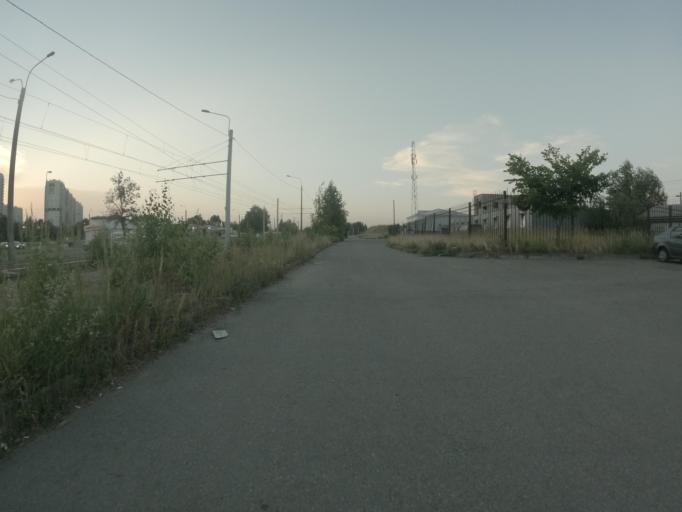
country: RU
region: St.-Petersburg
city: Krasnogvargeisky
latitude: 59.9339
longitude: 30.4427
